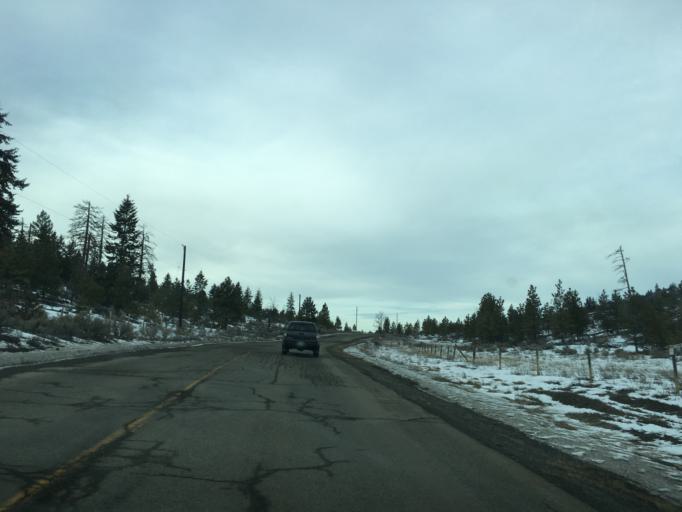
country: CA
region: British Columbia
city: Kamloops
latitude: 50.6374
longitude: -120.4486
